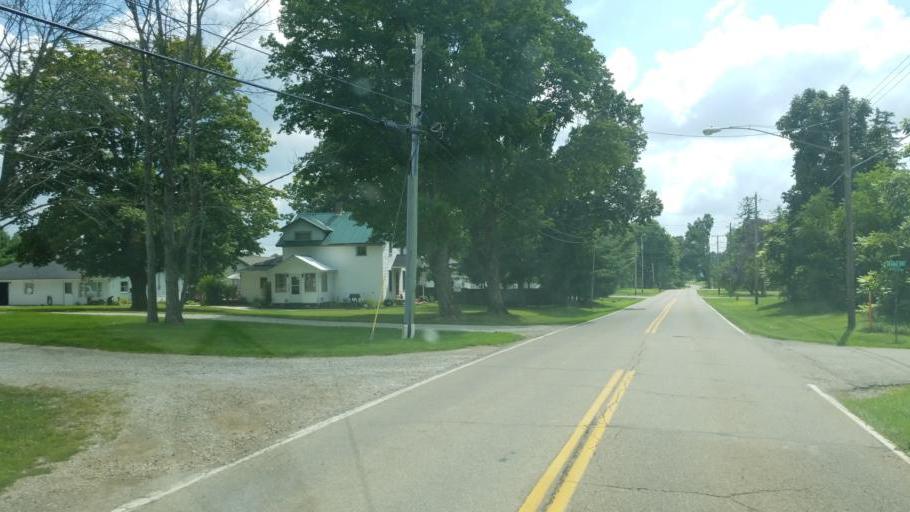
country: US
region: Ohio
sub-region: Knox County
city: Mount Vernon
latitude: 40.4181
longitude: -82.4886
